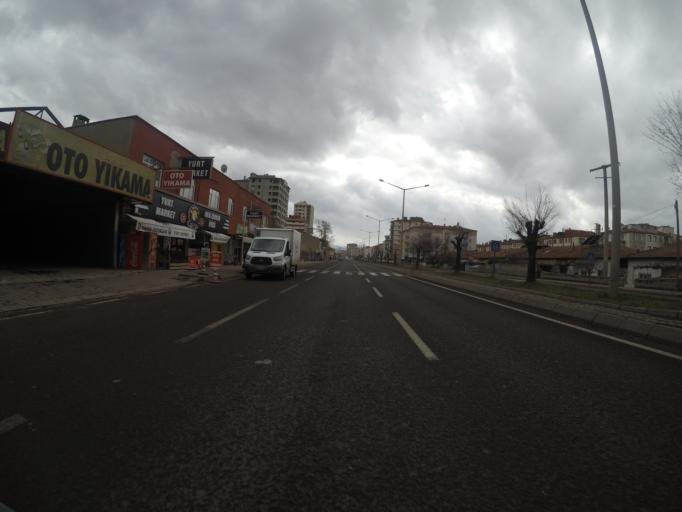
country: TR
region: Kayseri
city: Melikgazi
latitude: 38.7591
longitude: 35.4665
